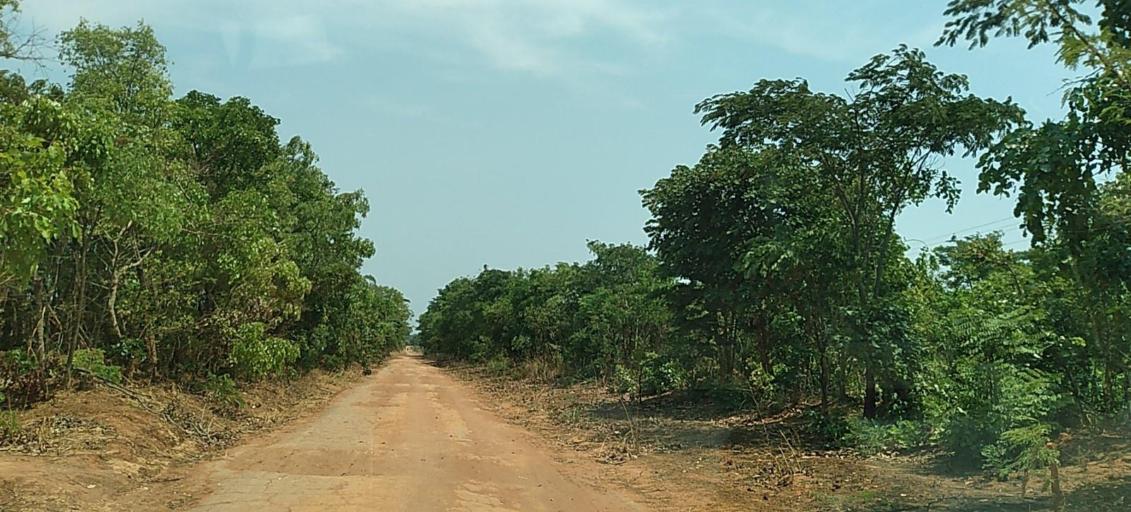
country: ZM
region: Copperbelt
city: Ndola
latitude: -13.0680
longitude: 28.7420
